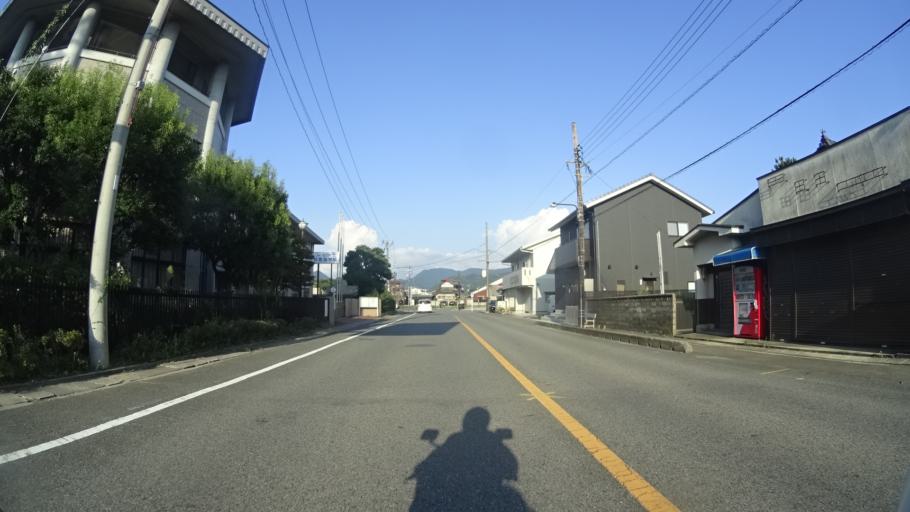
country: JP
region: Yamaguchi
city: Hagi
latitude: 34.4163
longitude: 131.3916
